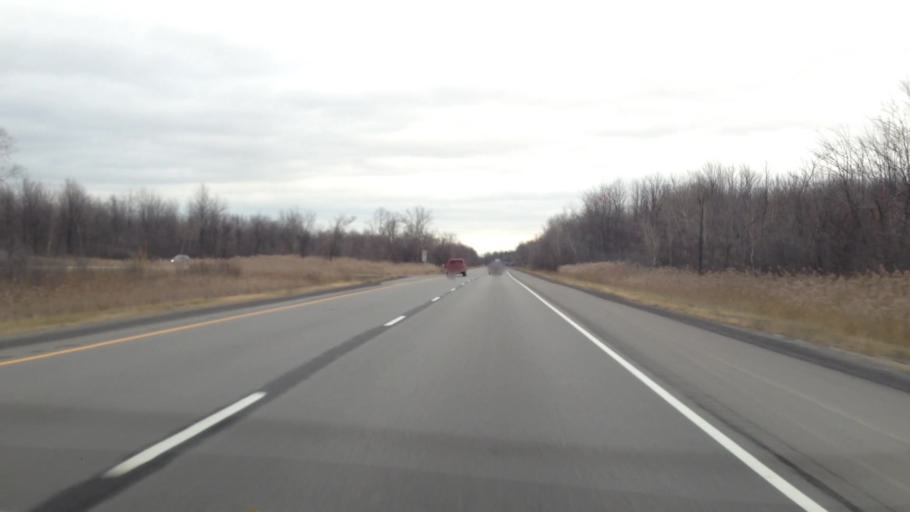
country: CA
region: Ontario
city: Bourget
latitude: 45.3224
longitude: -75.2755
